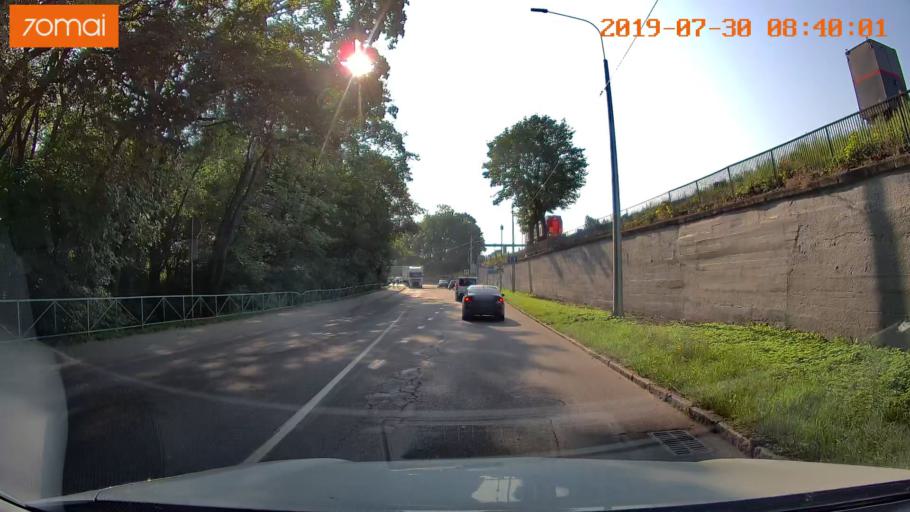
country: RU
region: Kaliningrad
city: Chernyakhovsk
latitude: 54.6302
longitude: 21.8086
